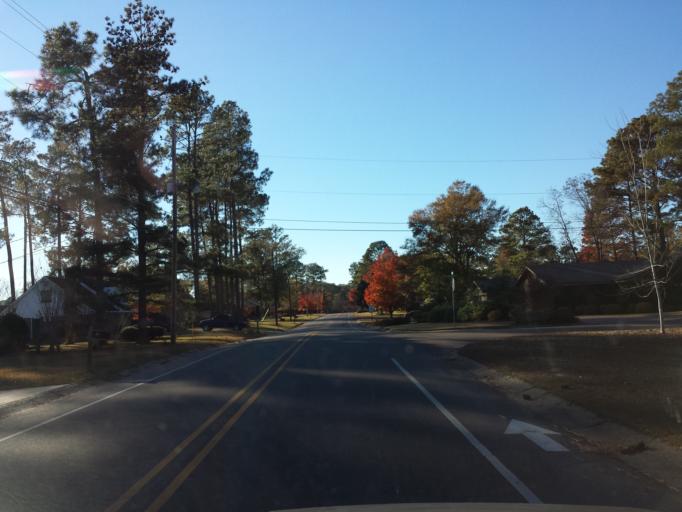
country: US
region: Mississippi
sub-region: Lamar County
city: West Hattiesburg
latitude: 31.3115
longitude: -89.3408
